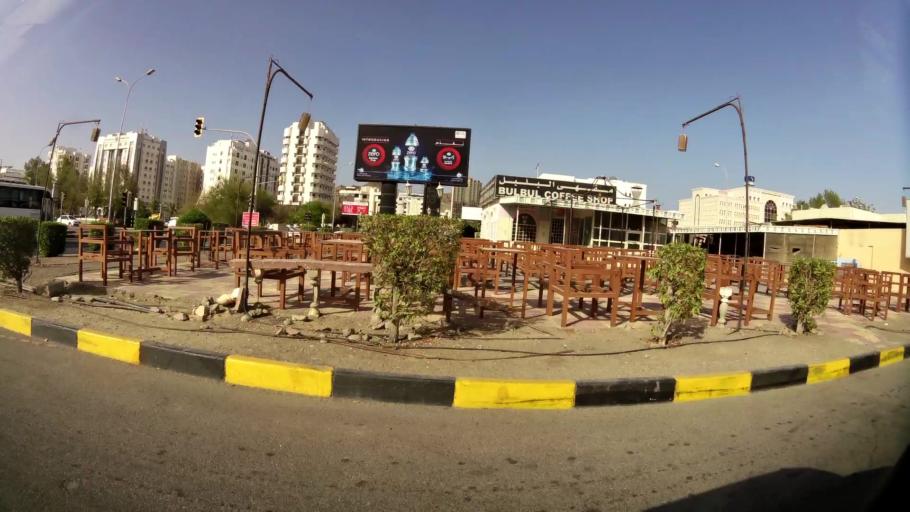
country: OM
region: Muhafazat Masqat
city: Muscat
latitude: 23.5952
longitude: 58.5469
